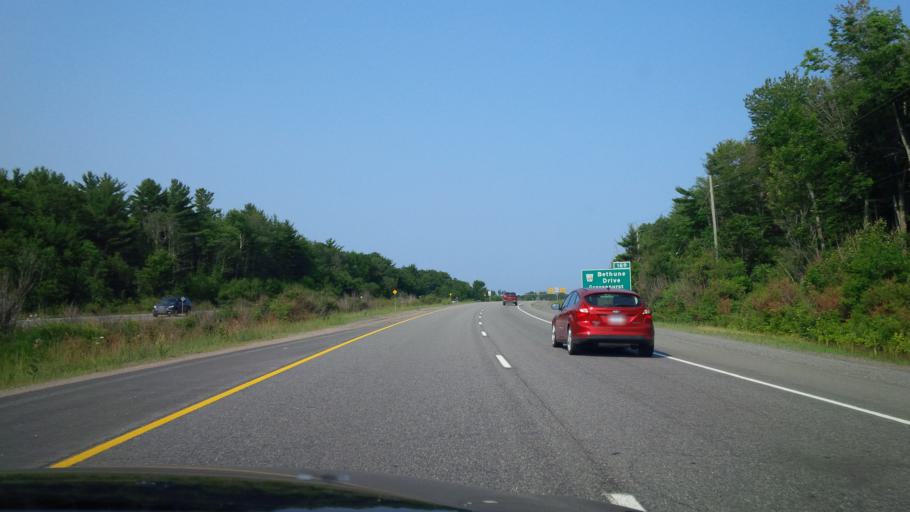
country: CA
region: Ontario
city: Gravenhurst
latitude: 44.9096
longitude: -79.3509
